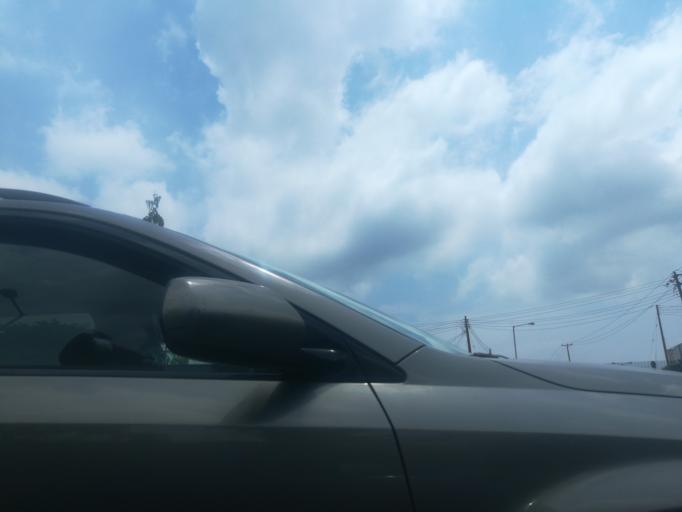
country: NG
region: Lagos
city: Ojota
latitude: 6.5746
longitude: 3.3973
